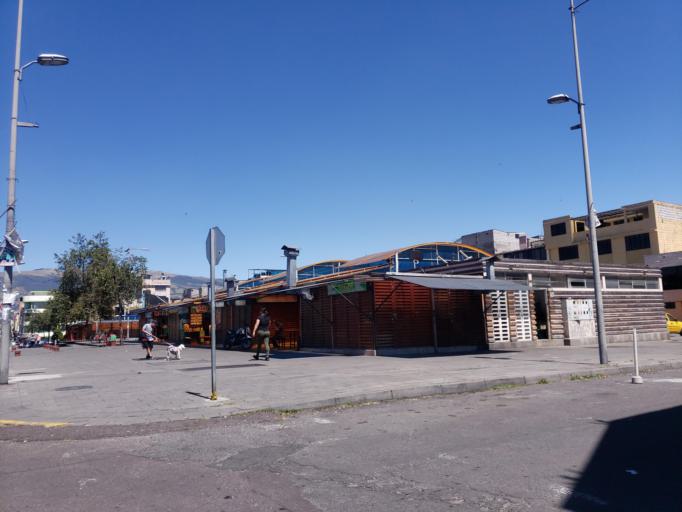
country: EC
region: Pichincha
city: Quito
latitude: -0.2660
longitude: -78.5372
